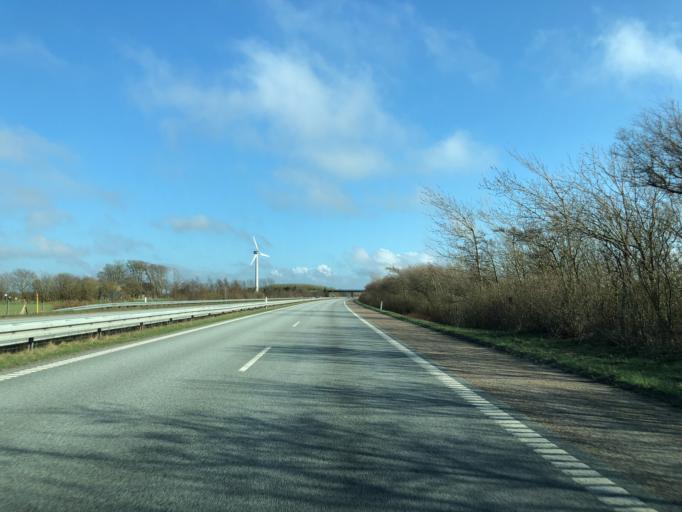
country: DK
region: North Denmark
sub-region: Hjorring Kommune
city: Hjorring
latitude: 57.4861
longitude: 10.0311
